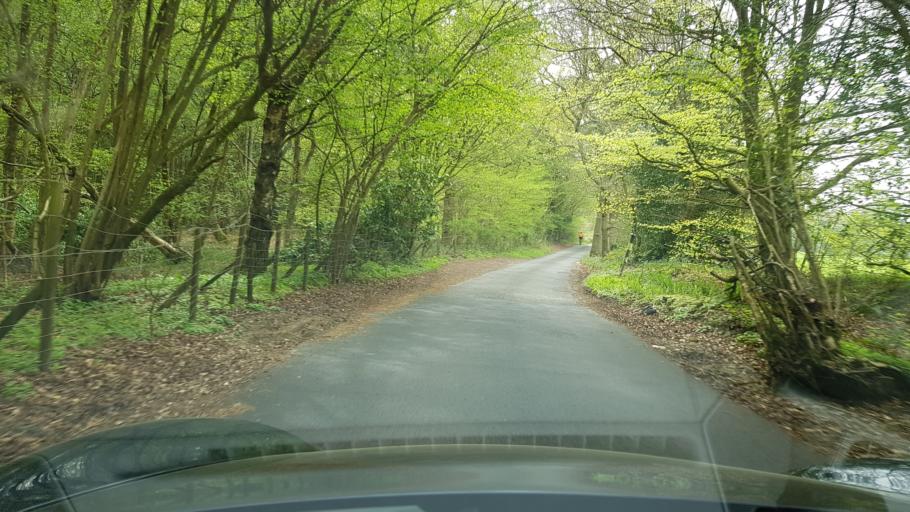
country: GB
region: England
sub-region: Surrey
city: East Horsley
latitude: 51.2387
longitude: -0.4514
